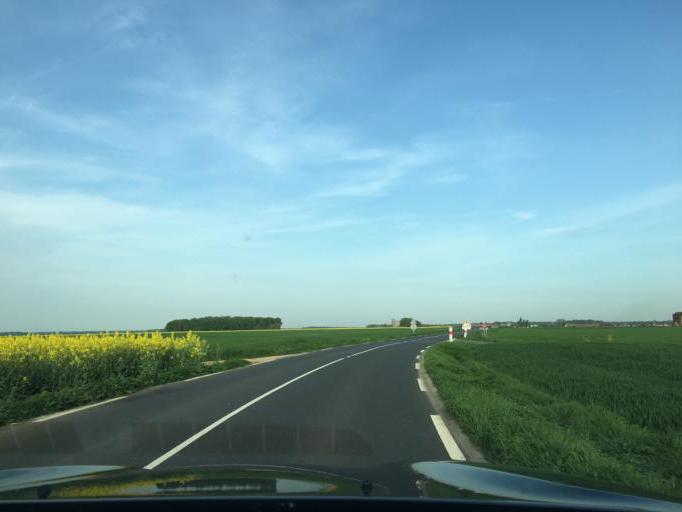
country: FR
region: Ile-de-France
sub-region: Departement des Yvelines
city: Sonchamp
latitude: 48.5781
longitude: 1.8289
